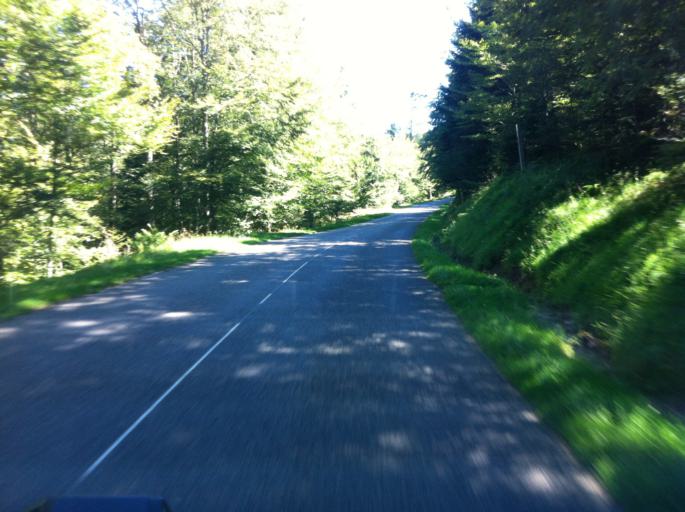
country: FR
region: Alsace
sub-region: Departement du Haut-Rhin
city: Soultzeren
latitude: 48.1232
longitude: 7.0684
